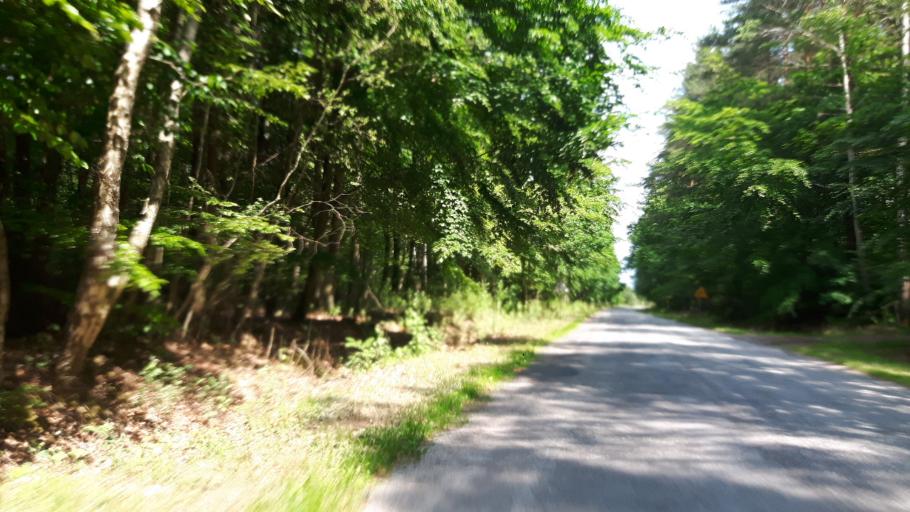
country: PL
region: West Pomeranian Voivodeship
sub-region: Powiat goleniowski
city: Osina
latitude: 53.6532
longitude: 14.9626
